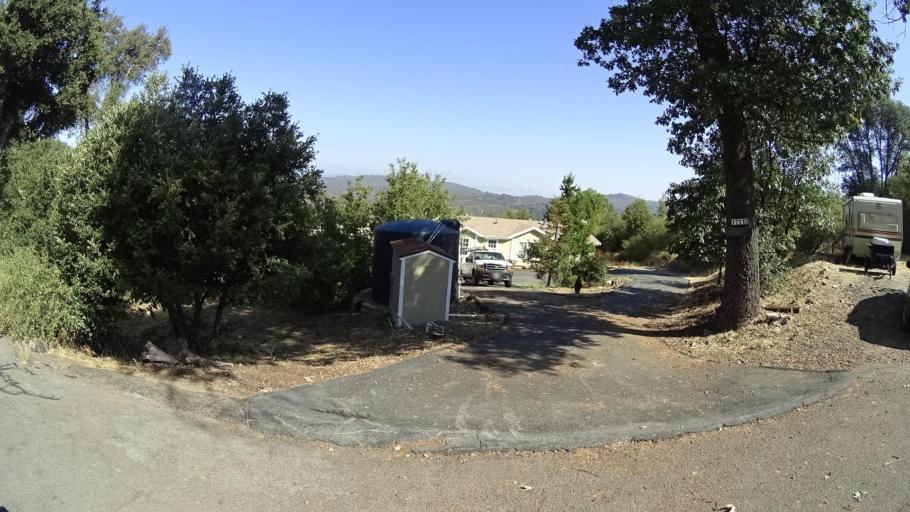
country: US
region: California
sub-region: San Diego County
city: Julian
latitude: 33.0210
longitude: -116.5774
